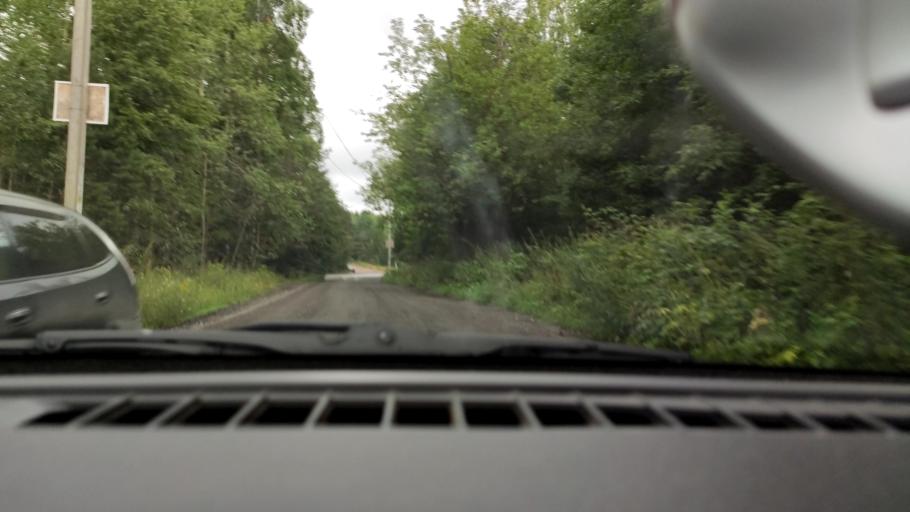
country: RU
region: Perm
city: Kondratovo
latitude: 58.0516
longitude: 55.9975
